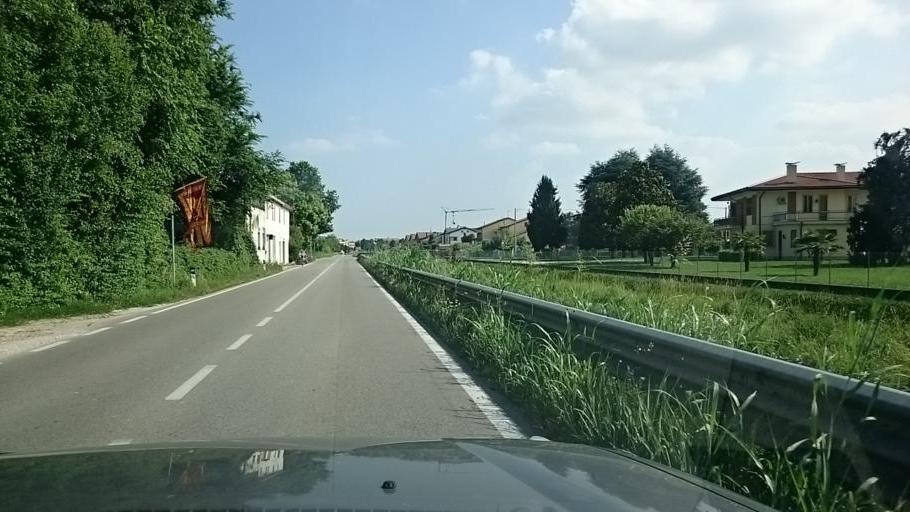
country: IT
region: Veneto
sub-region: Provincia di Padova
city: San Giorgio delle Pertiche
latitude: 45.5487
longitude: 11.8737
